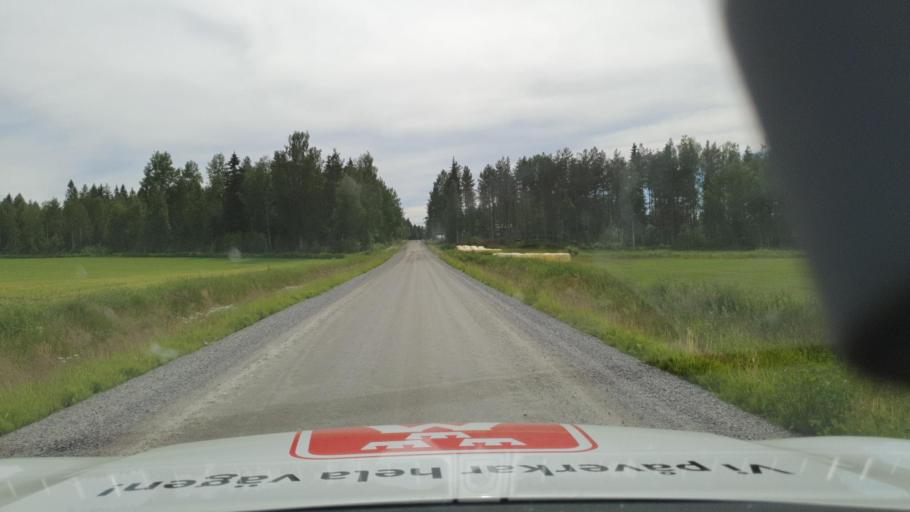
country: SE
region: Vaesterbotten
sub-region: Skelleftea Kommun
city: Burea
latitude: 64.4695
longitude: 21.0565
